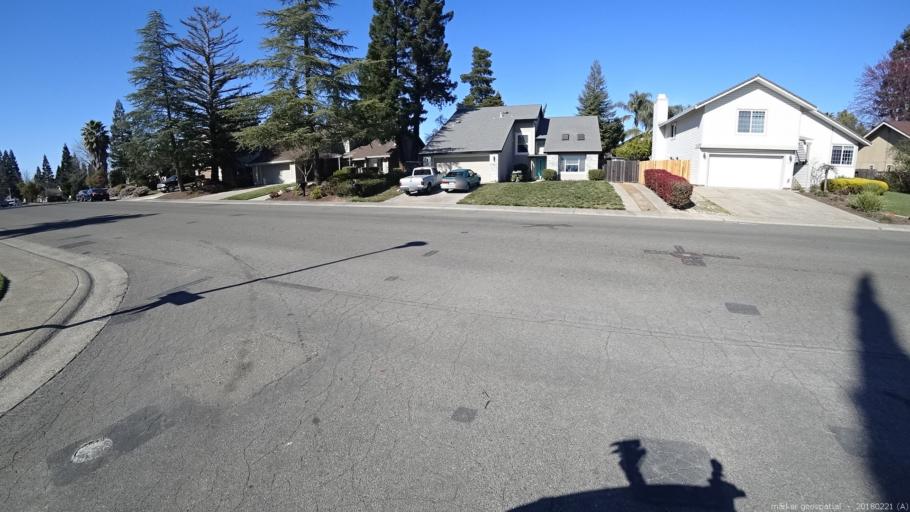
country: US
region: California
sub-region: Sacramento County
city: Citrus Heights
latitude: 38.6836
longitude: -121.2596
